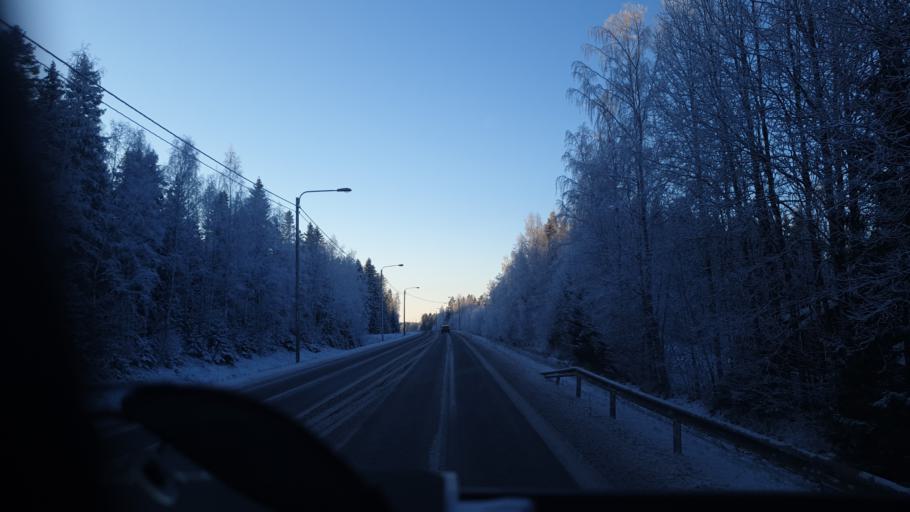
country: FI
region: Central Ostrobothnia
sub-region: Kokkola
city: Kaelviae
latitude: 63.9233
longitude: 23.4184
